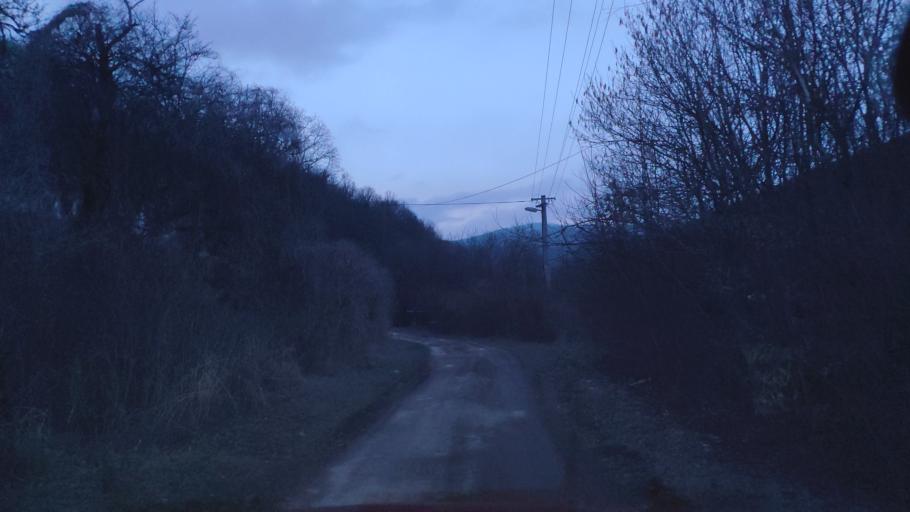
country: SK
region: Kosicky
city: Medzev
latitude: 48.7161
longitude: 20.9247
